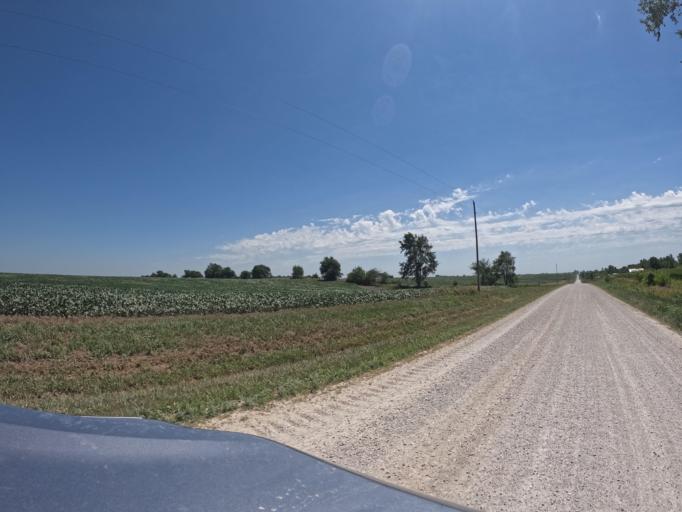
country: US
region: Iowa
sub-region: Keokuk County
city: Sigourney
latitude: 41.4133
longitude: -92.3164
